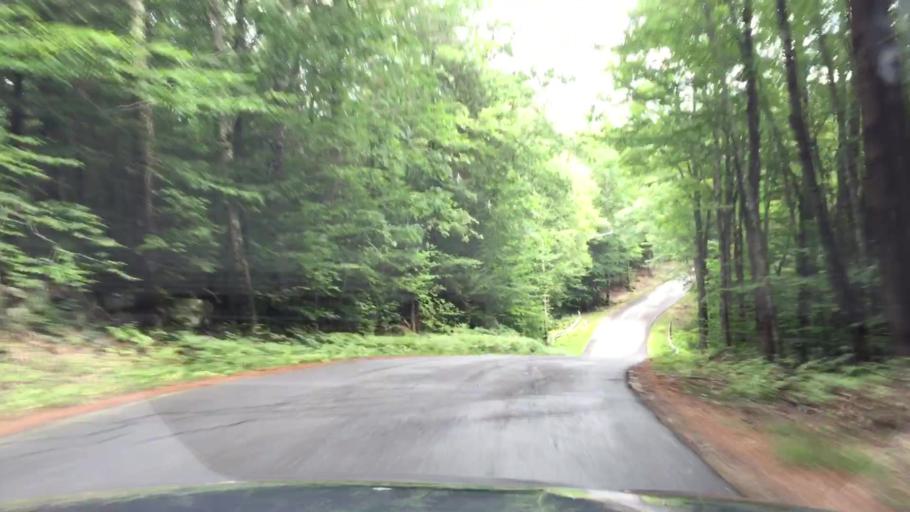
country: US
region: New Hampshire
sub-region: Carroll County
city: Sandwich
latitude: 43.7943
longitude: -71.4773
